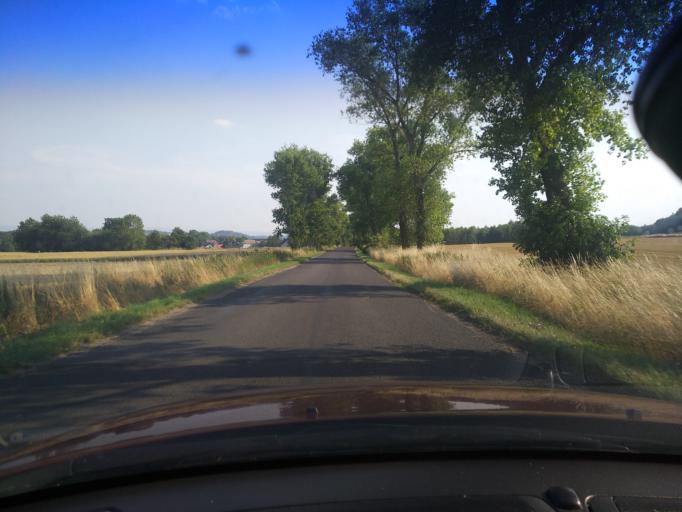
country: PL
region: Lower Silesian Voivodeship
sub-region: Powiat zgorzelecki
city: Sulikow
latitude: 51.1110
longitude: 15.0668
